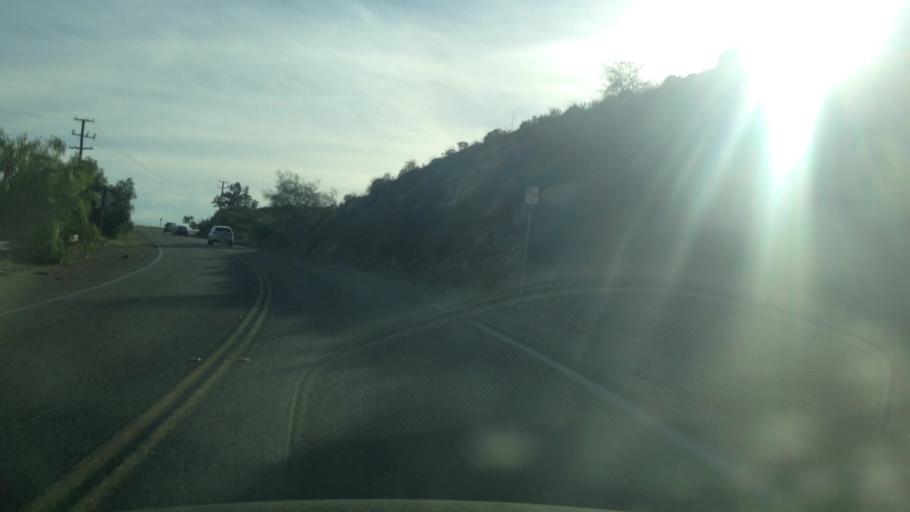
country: US
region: California
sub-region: Riverside County
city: El Cerrito
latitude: 33.8557
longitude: -117.4544
